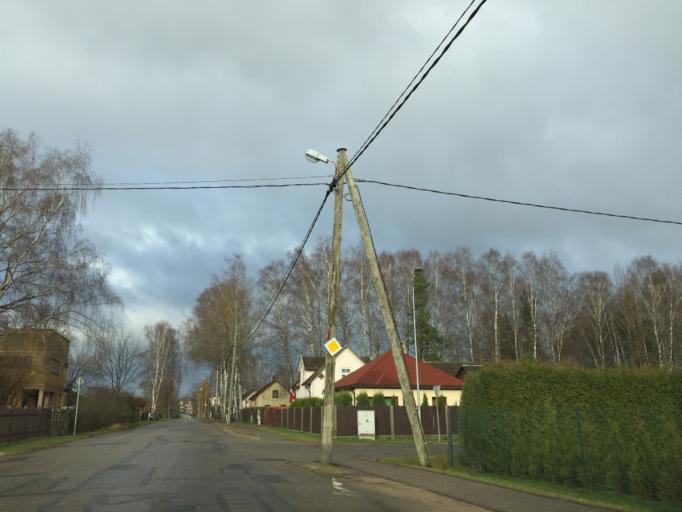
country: LV
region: Valmieras Rajons
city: Valmiera
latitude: 57.5260
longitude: 25.4280
